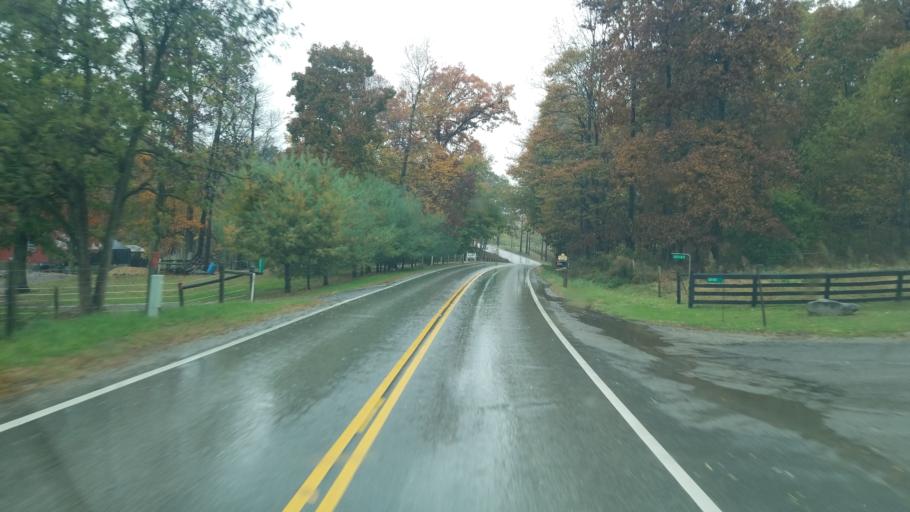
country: US
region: Ohio
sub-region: Coshocton County
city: West Lafayette
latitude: 40.4190
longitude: -81.7999
